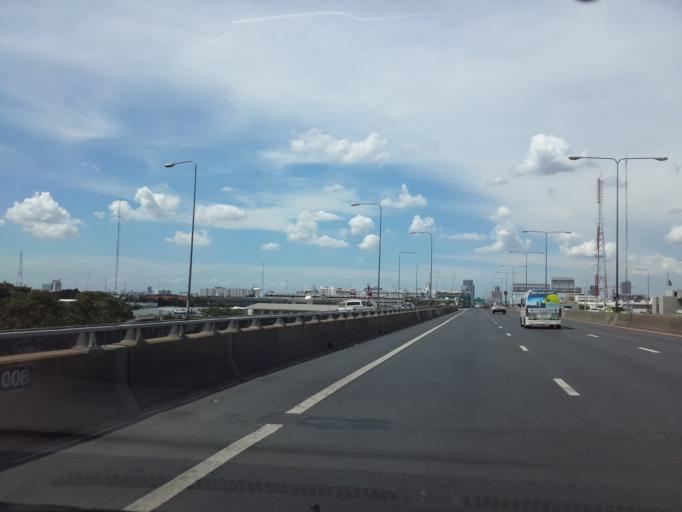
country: TH
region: Bangkok
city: Ratchathewi
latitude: 13.7584
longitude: 100.5242
